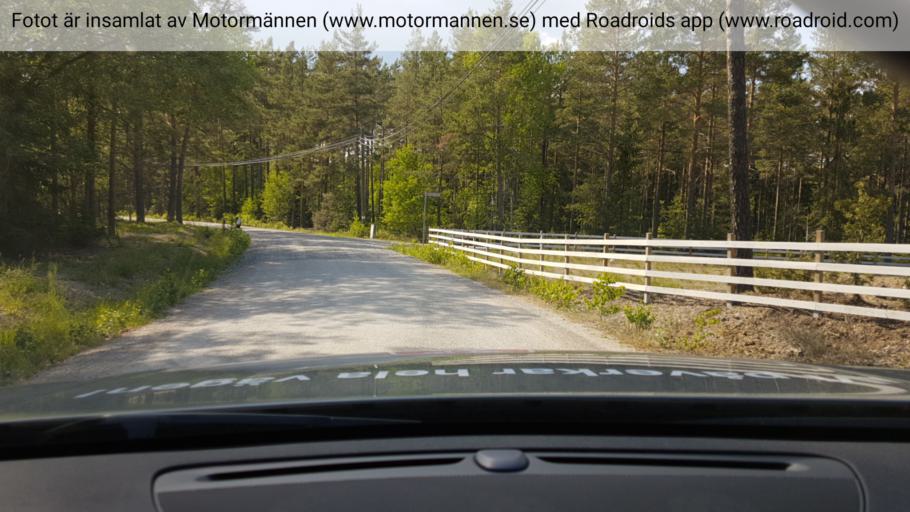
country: SE
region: Stockholm
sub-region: Varmdo Kommun
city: Mortnas
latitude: 59.2578
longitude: 18.4362
